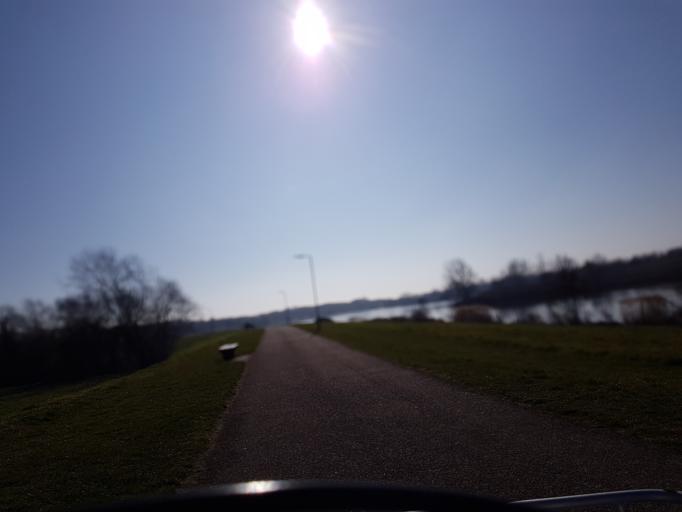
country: GB
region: England
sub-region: Milton Keynes
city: Broughton
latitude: 52.0606
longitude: -0.7181
